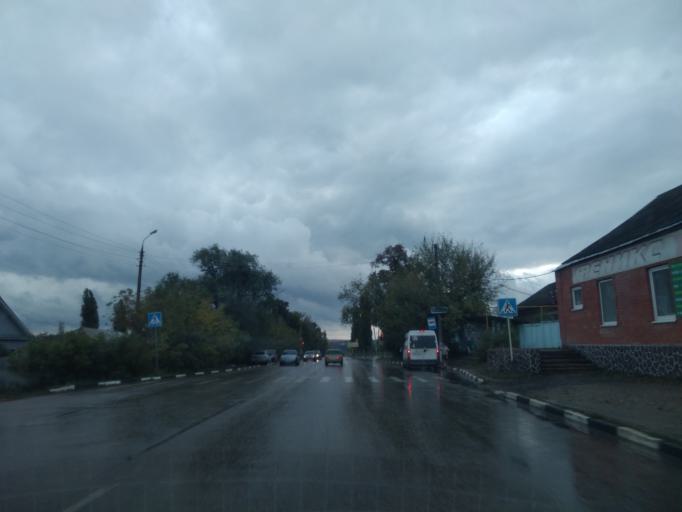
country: RU
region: Tula
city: Yefremov
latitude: 53.1336
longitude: 38.1174
